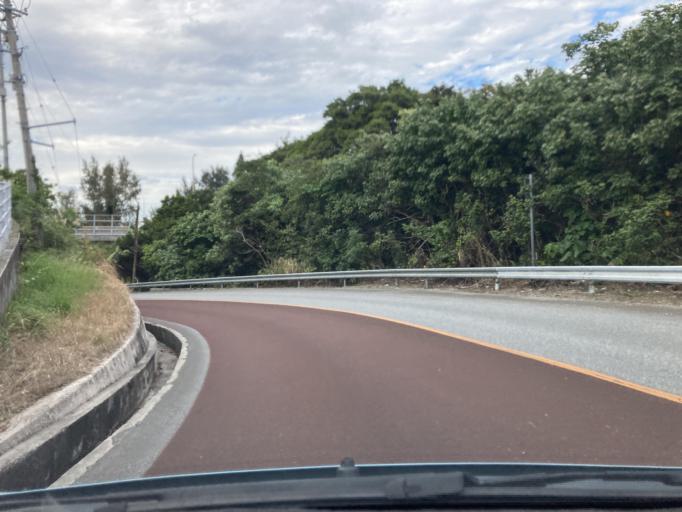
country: JP
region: Okinawa
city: Ishikawa
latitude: 26.4377
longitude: 127.8054
